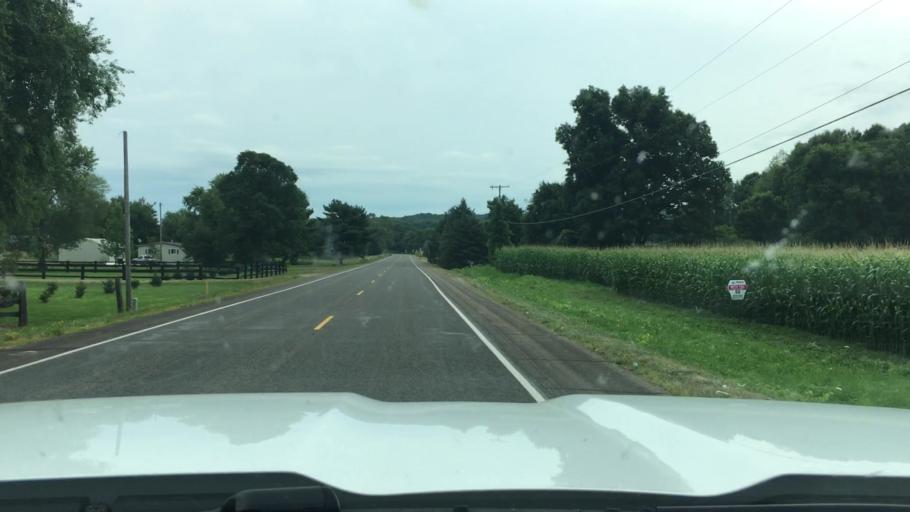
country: US
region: Michigan
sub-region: Allegan County
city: Plainwell
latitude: 42.4648
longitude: -85.6088
